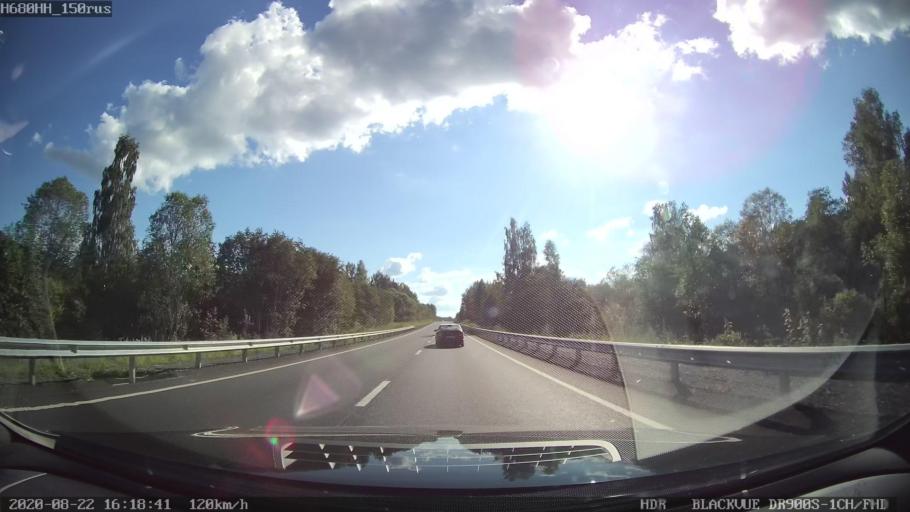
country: RU
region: Tverskaya
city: Rameshki
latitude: 57.4133
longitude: 36.1350
